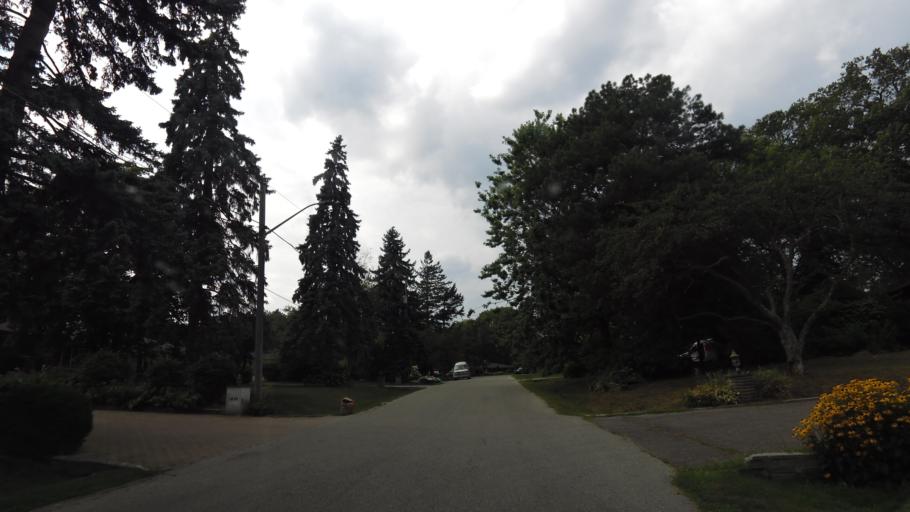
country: CA
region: Ontario
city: Mississauga
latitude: 43.5568
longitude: -79.6074
